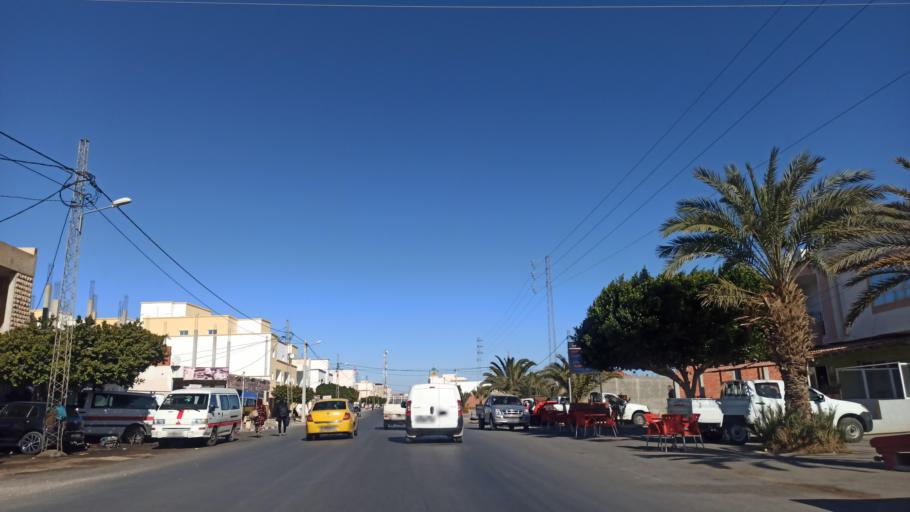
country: TN
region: Sidi Bu Zayd
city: Bi'r al Hufayy
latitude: 34.9232
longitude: 9.1893
